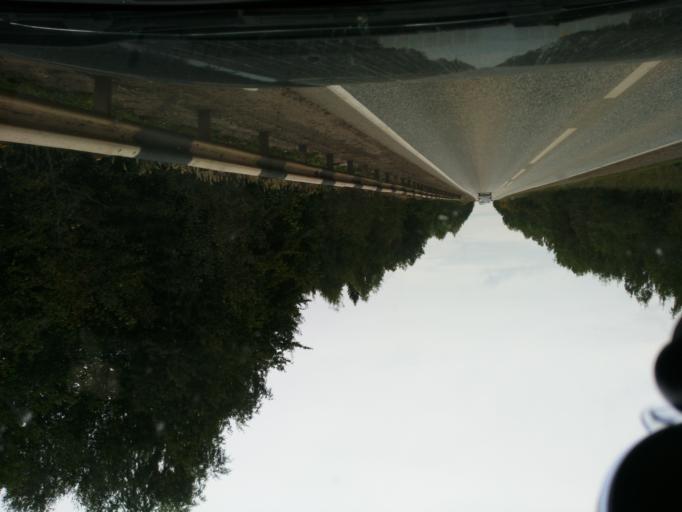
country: RU
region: Perm
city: Chernushka
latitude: 56.5811
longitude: 56.1410
